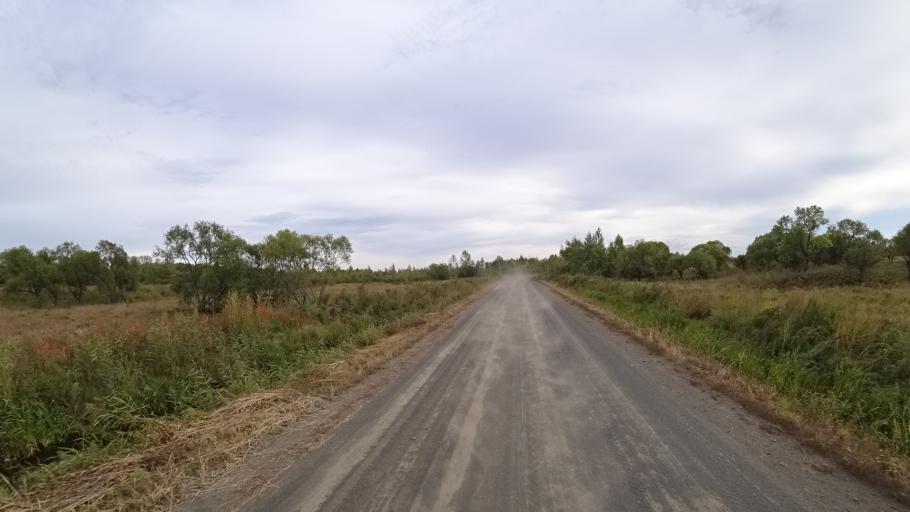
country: RU
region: Amur
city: Arkhara
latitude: 49.3174
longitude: 130.1828
